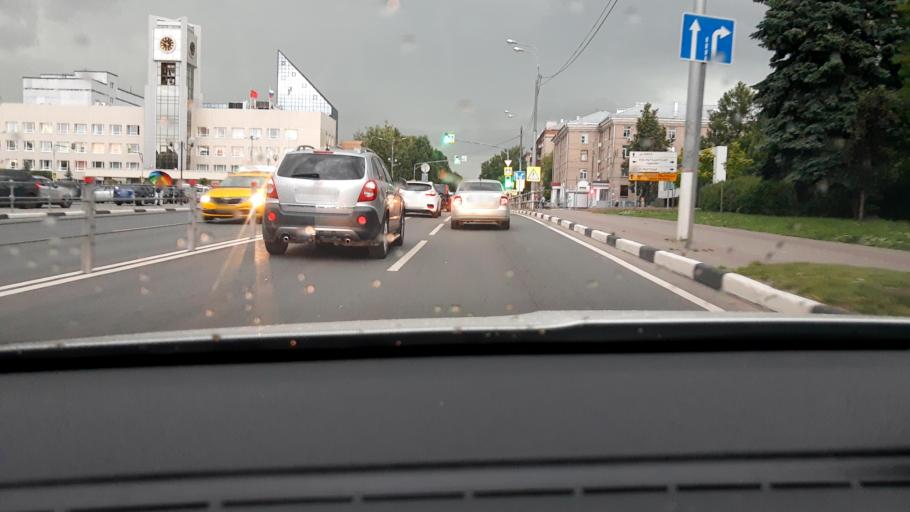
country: RU
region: Moskovskaya
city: Mytishchi
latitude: 55.9099
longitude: 37.7377
